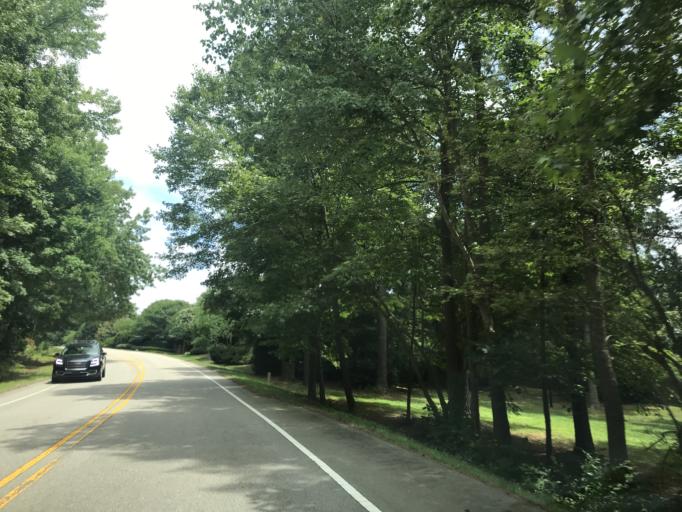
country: US
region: North Carolina
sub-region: Wake County
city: West Raleigh
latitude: 35.9109
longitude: -78.6738
